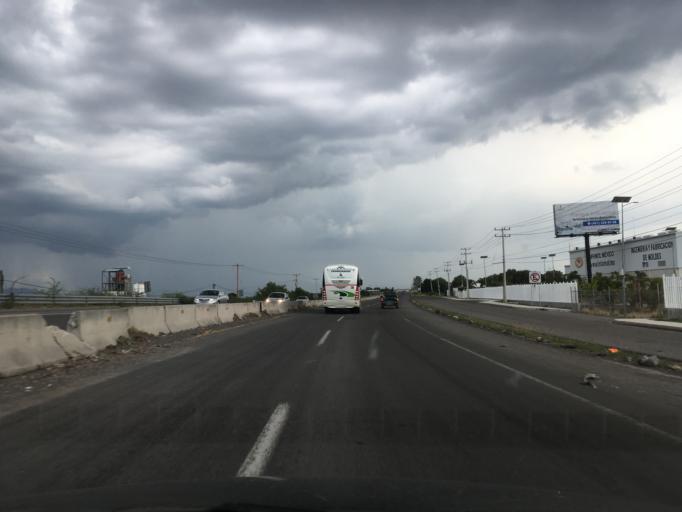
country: MX
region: Guanajuato
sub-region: Celaya
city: El Sauz (El Sauz de Villasenor)
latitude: 20.3980
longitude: -100.7888
